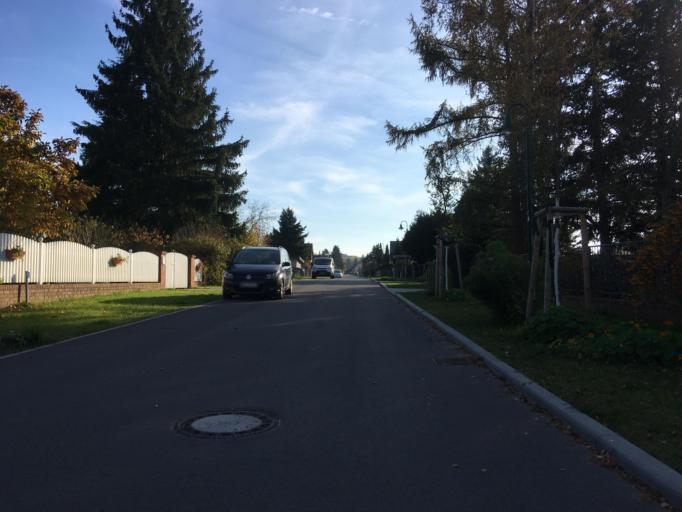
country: DE
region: Berlin
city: Buch
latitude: 52.6491
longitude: 13.5406
